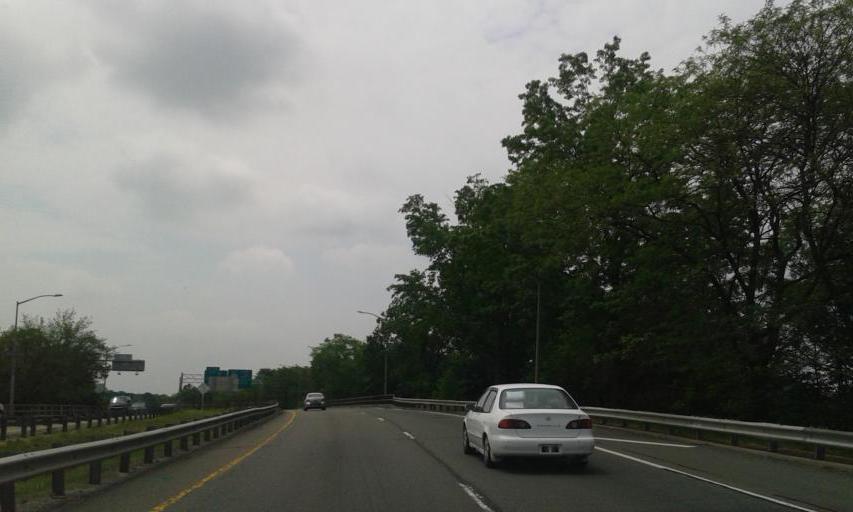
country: US
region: New York
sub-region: Richmond County
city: Bloomfield
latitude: 40.6185
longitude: -74.1514
